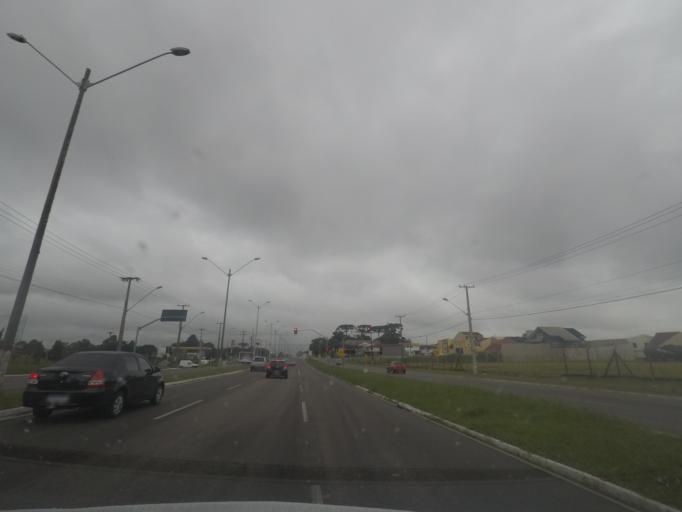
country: BR
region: Parana
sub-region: Pinhais
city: Pinhais
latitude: -25.3864
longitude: -49.2038
